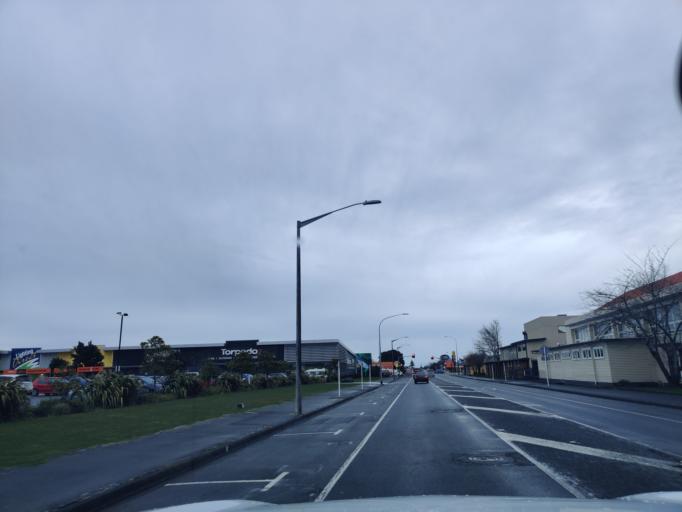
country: NZ
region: Manawatu-Wanganui
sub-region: Palmerston North City
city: Palmerston North
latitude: -40.3490
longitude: 175.6083
